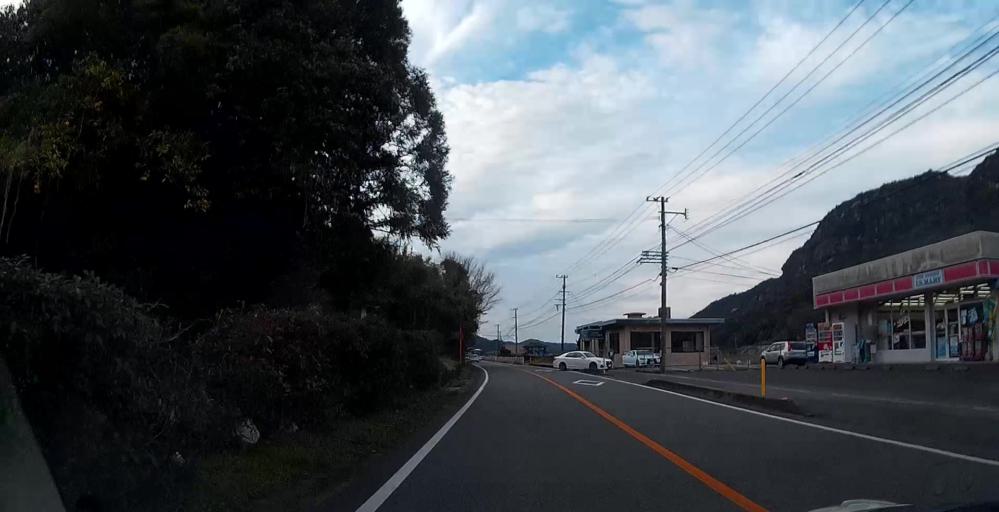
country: JP
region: Kumamoto
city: Yatsushiro
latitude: 32.4961
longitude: 130.4115
